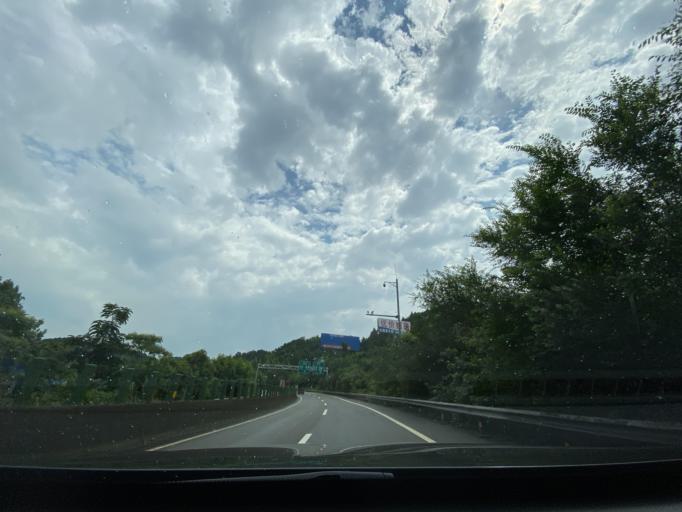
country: CN
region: Sichuan
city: Yanjiang
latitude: 30.2182
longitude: 104.6024
